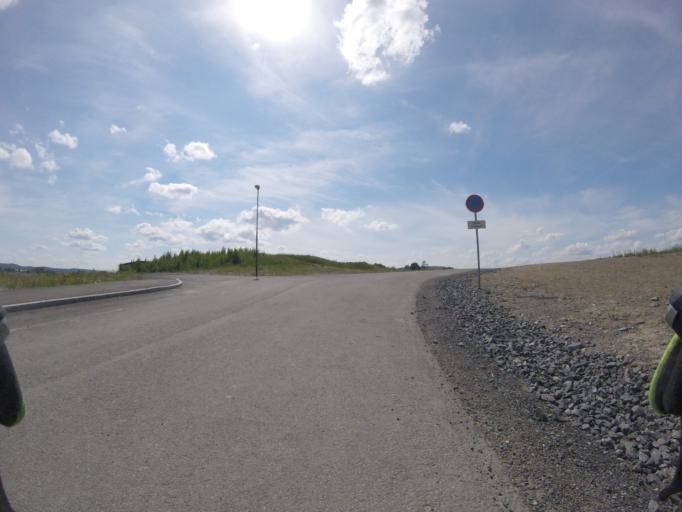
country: NO
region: Akershus
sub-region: Skedsmo
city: Lillestrom
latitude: 59.9775
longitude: 11.0377
